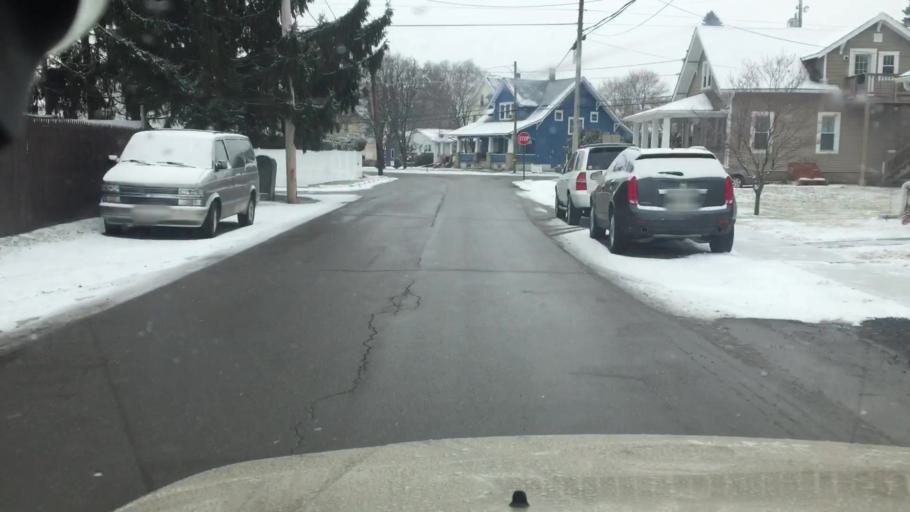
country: US
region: Pennsylvania
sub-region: Columbia County
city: Berwick
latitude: 41.0706
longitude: -76.2392
